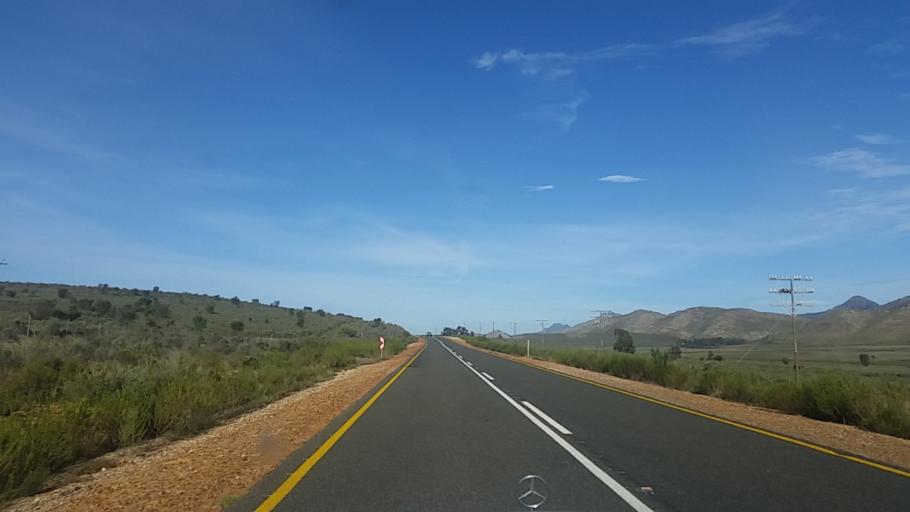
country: ZA
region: Western Cape
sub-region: Eden District Municipality
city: George
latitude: -33.7739
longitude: 22.7468
